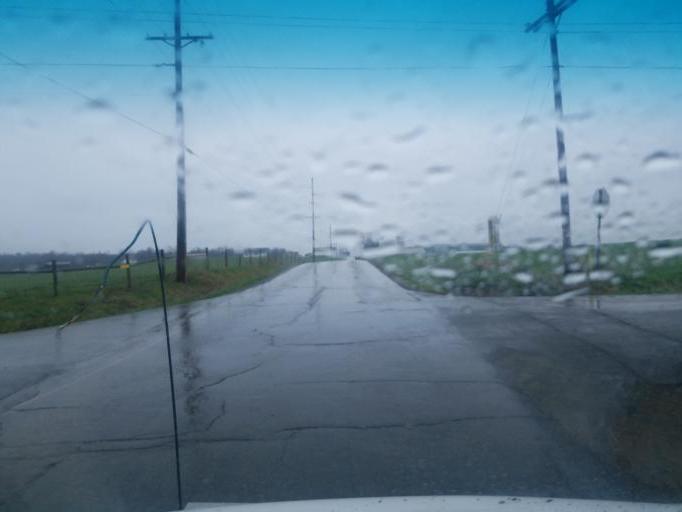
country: US
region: Ohio
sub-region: Wayne County
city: Apple Creek
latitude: 40.7110
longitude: -81.9057
